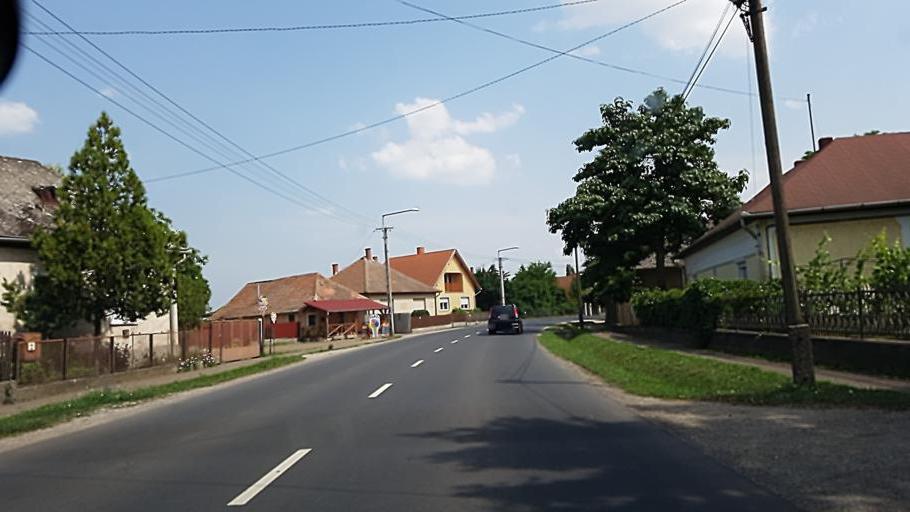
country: HU
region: Heves
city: Besenyotelek
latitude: 47.6967
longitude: 20.4316
